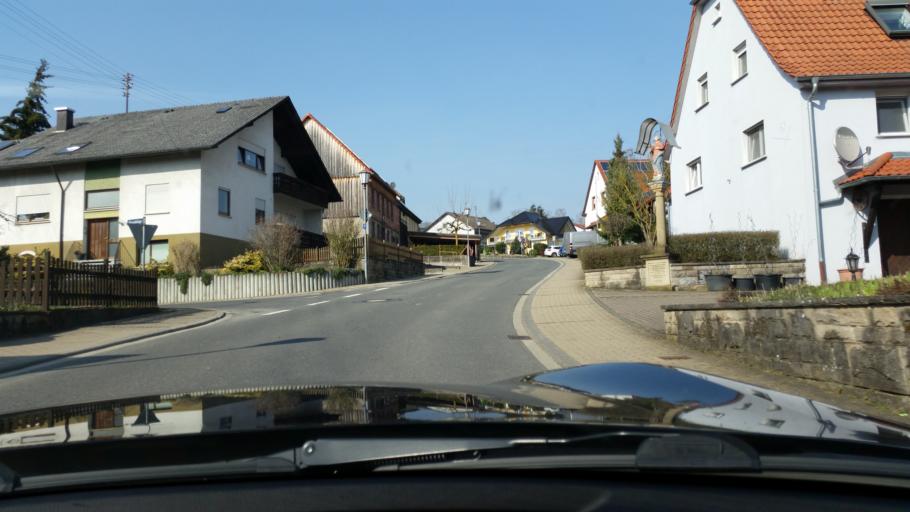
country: DE
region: Baden-Wuerttemberg
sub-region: Karlsruhe Region
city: Billigheim
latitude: 49.3632
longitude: 9.2815
